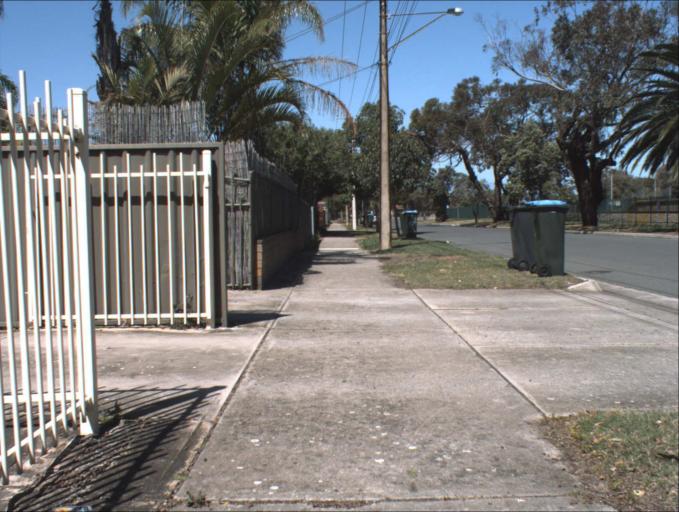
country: AU
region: South Australia
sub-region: Port Adelaide Enfield
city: Birkenhead
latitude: -34.8146
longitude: 138.4993
